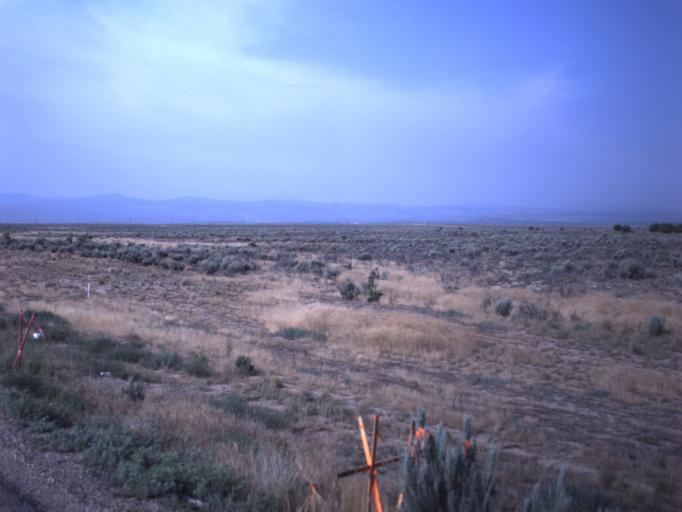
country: US
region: Utah
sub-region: Duchesne County
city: Duchesne
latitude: 40.2713
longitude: -110.3809
